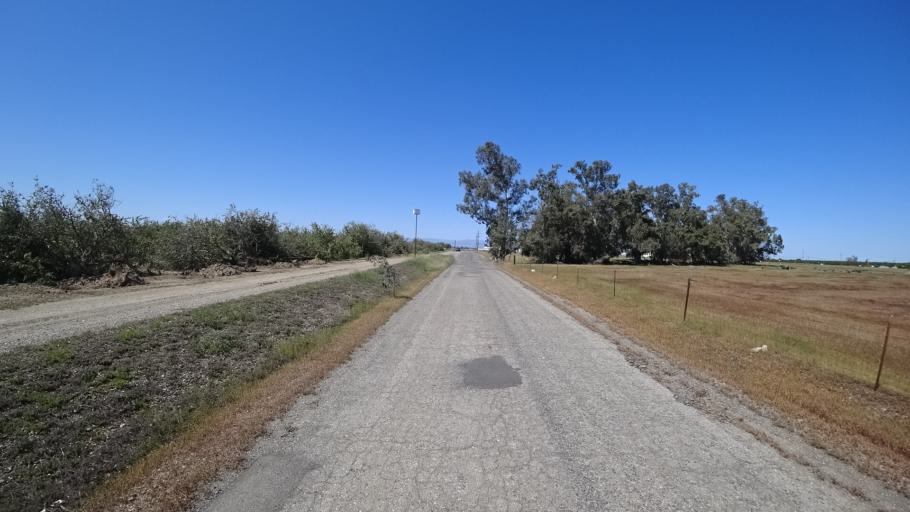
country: US
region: California
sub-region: Glenn County
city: Orland
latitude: 39.7216
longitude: -122.1384
